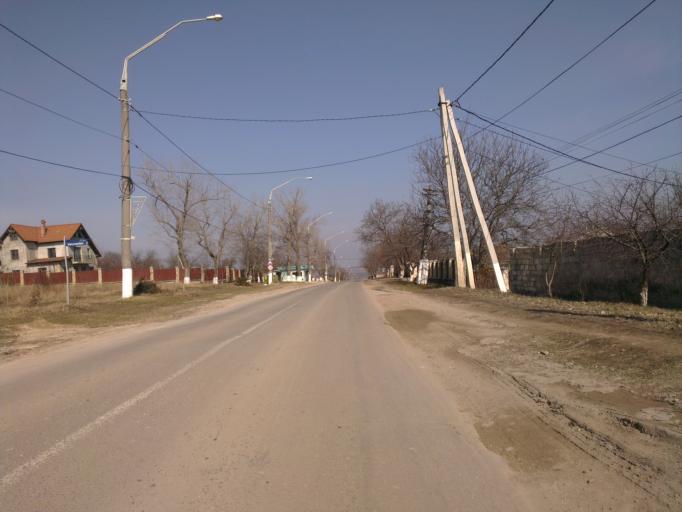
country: MD
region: Chisinau
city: Cricova
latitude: 47.1289
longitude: 28.8648
